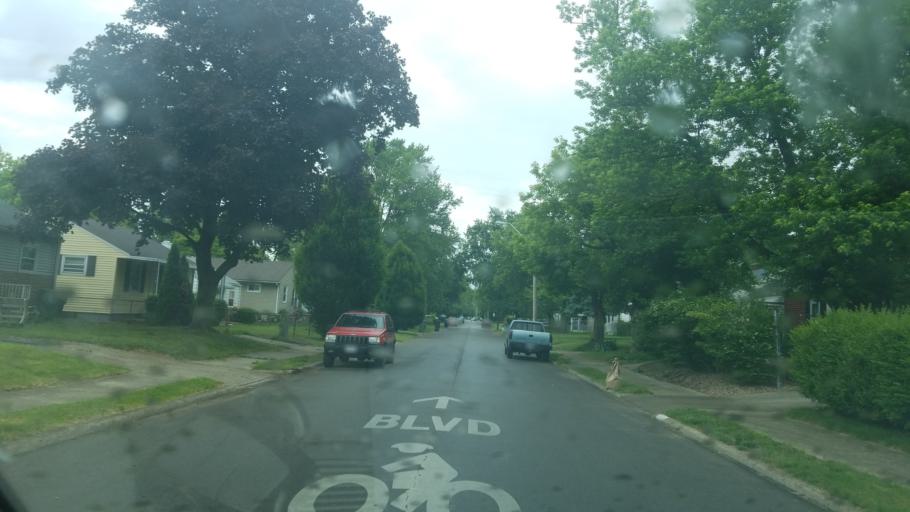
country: US
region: Ohio
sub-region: Franklin County
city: Columbus
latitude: 40.0210
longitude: -82.9863
